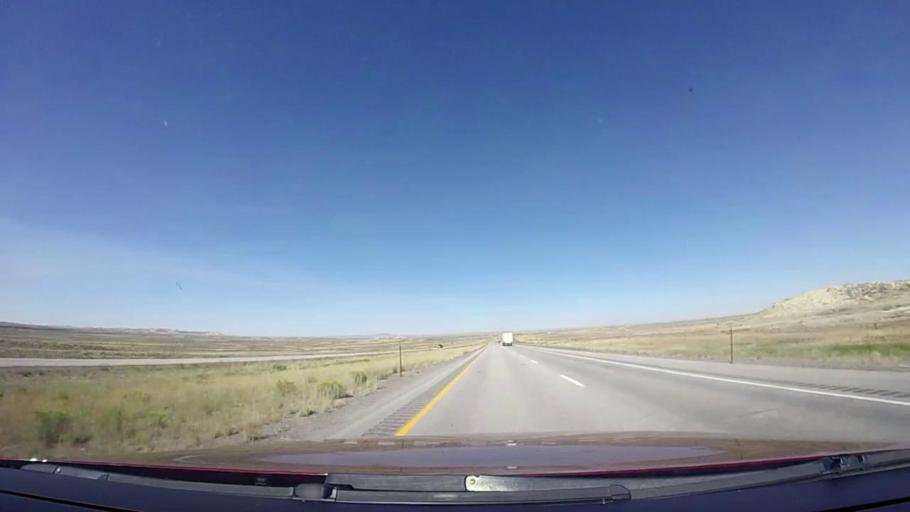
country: US
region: Wyoming
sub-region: Sweetwater County
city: Rock Springs
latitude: 41.6321
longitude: -108.3547
